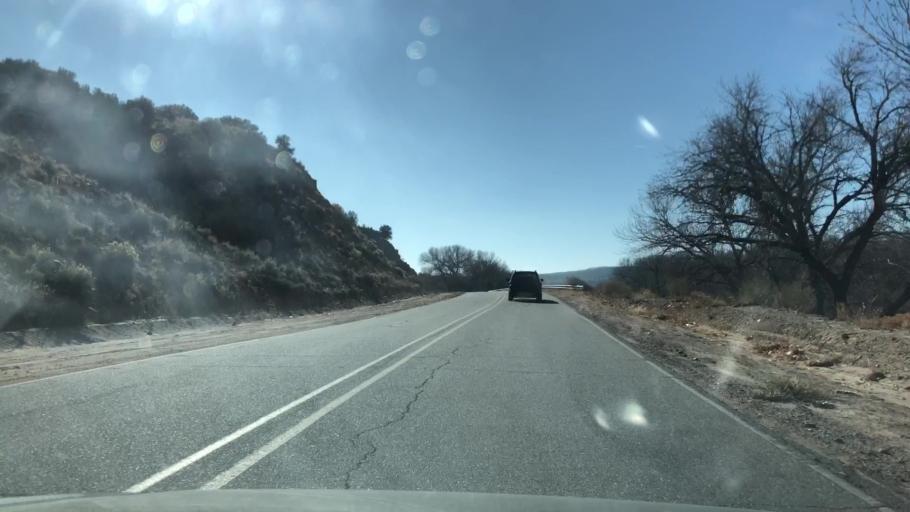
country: US
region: New Mexico
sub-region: Rio Arriba County
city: Ohkay Owingeh
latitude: 36.0933
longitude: -106.1297
